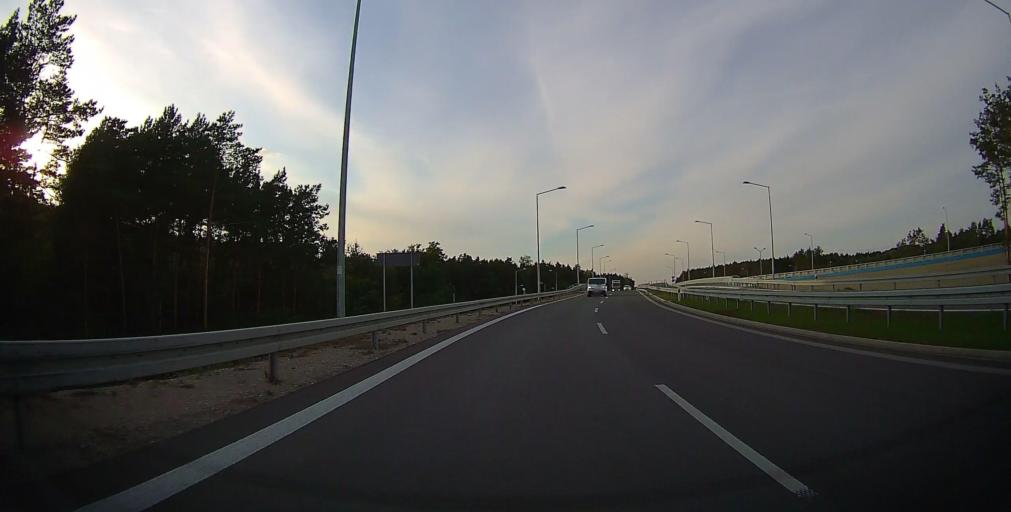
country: PL
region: Masovian Voivodeship
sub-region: Powiat piaseczynski
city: Gora Kalwaria
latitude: 51.9695
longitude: 21.1961
